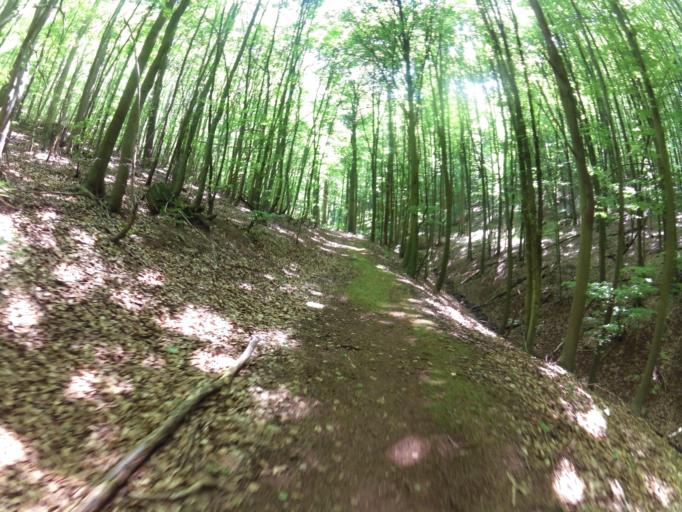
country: DE
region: Thuringia
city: Eisenach
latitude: 50.9650
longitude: 10.3027
